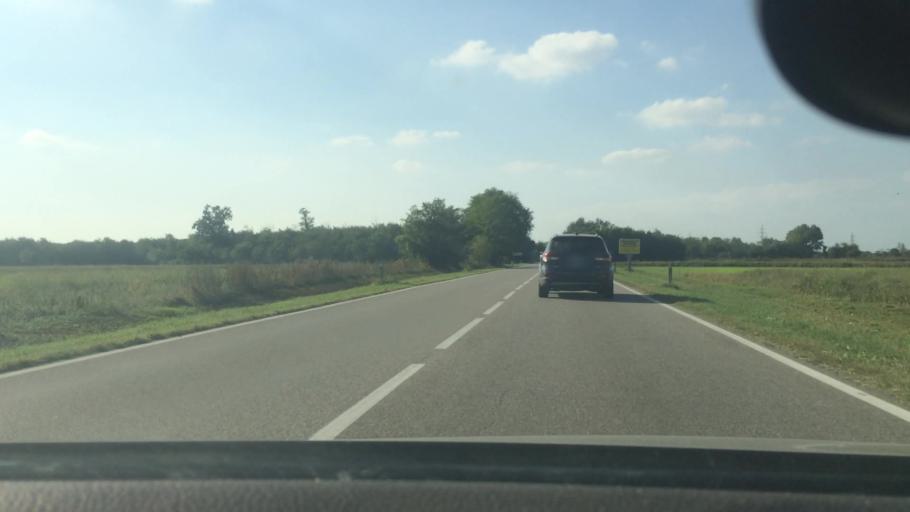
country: IT
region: Lombardy
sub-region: Citta metropolitana di Milano
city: Inveruno
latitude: 45.5258
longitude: 8.8472
